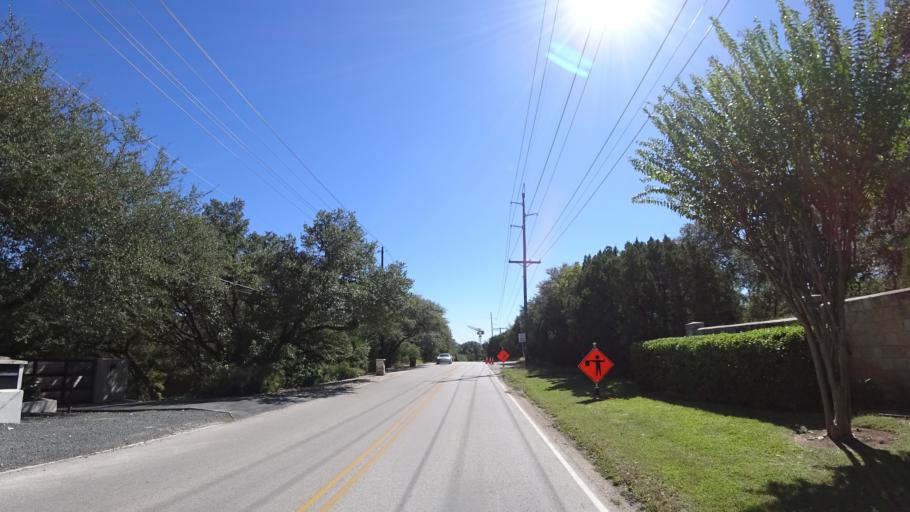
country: US
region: Texas
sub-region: Travis County
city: West Lake Hills
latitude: 30.3256
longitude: -97.7802
